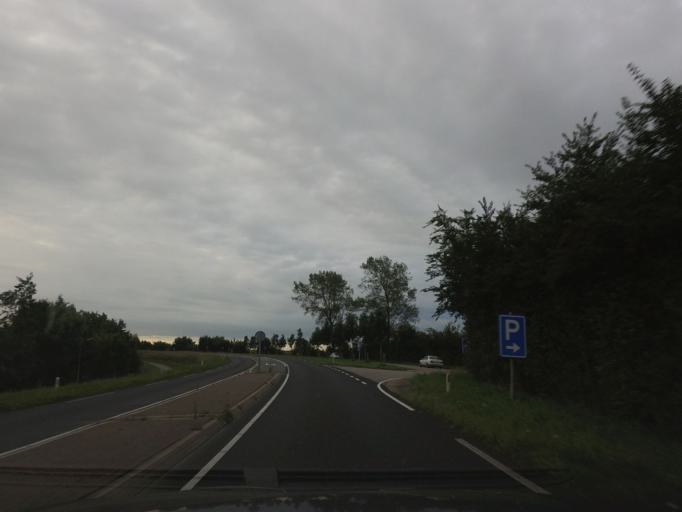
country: NL
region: North Holland
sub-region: Gemeente Uitgeest
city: Uitgeest
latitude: 52.5683
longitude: 4.7458
